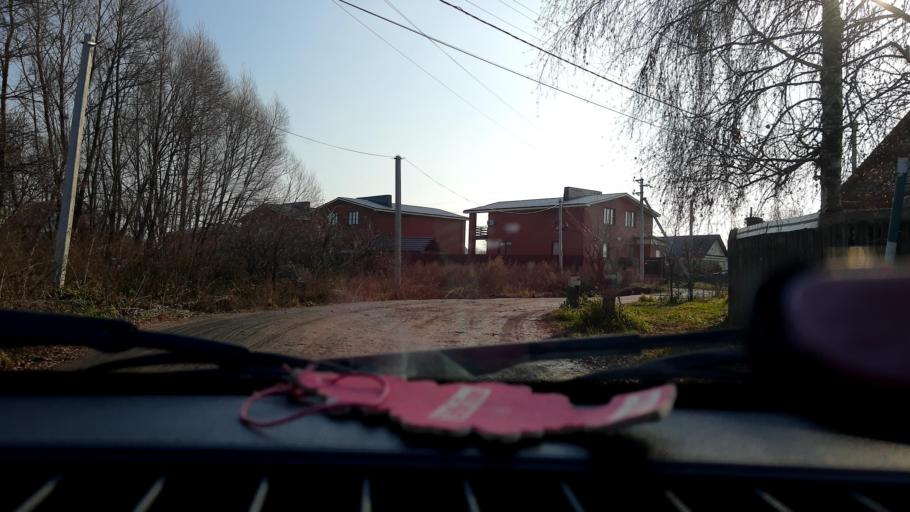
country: RU
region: Bashkortostan
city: Ufa
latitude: 54.6756
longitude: 56.0857
